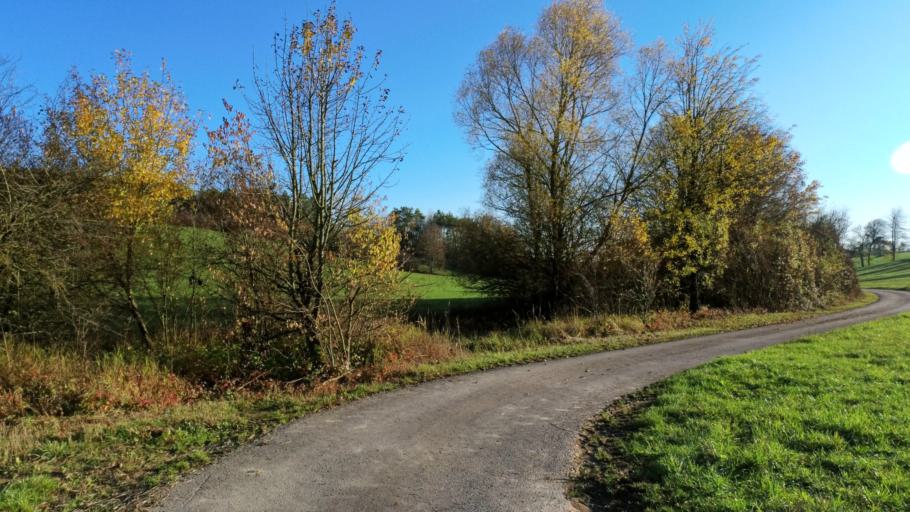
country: DE
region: Baden-Wuerttemberg
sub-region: Karlsruhe Region
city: Limbach
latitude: 49.4305
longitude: 9.2498
